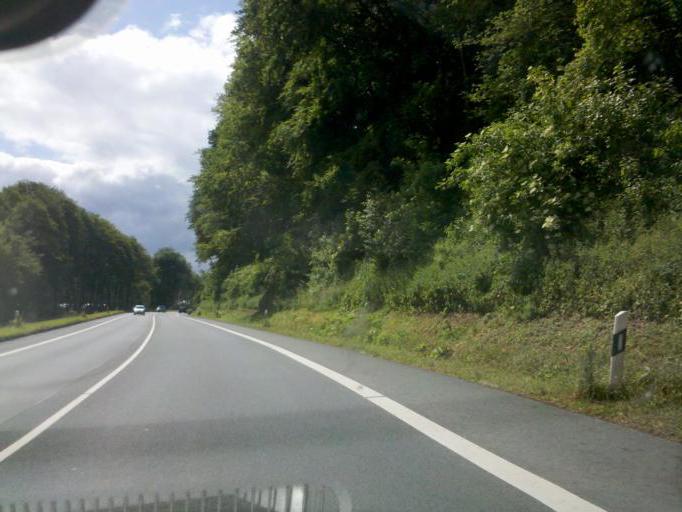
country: DE
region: North Rhine-Westphalia
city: Warstein
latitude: 51.4632
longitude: 8.3404
